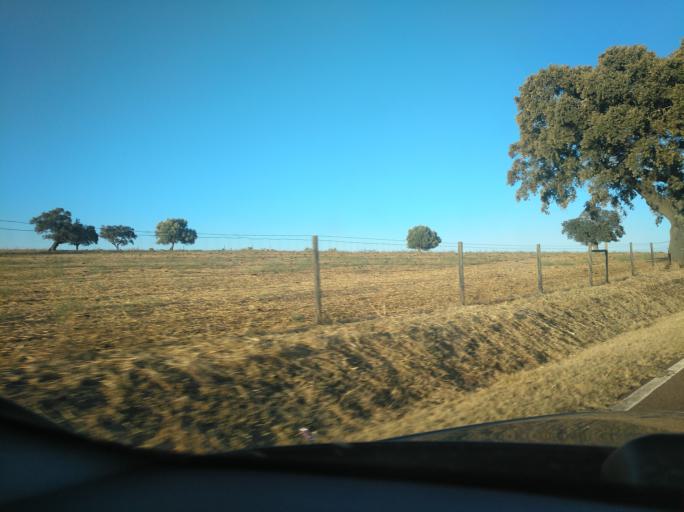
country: PT
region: Portalegre
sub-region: Arronches
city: Arronches
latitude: 39.0693
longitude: -7.1869
